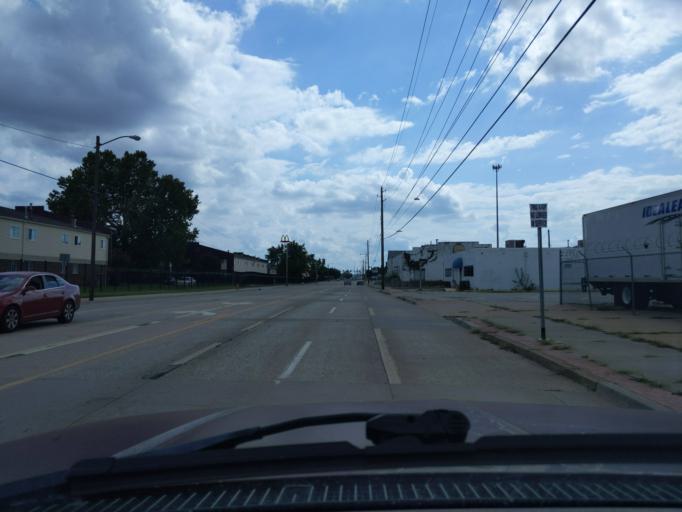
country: US
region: Oklahoma
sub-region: Tulsa County
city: Tulsa
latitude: 36.1333
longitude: -96.0070
